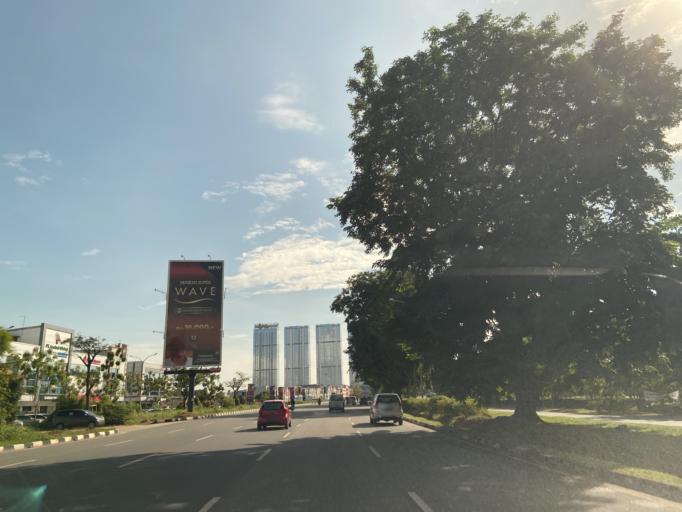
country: SG
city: Singapore
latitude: 1.1116
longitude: 104.0421
